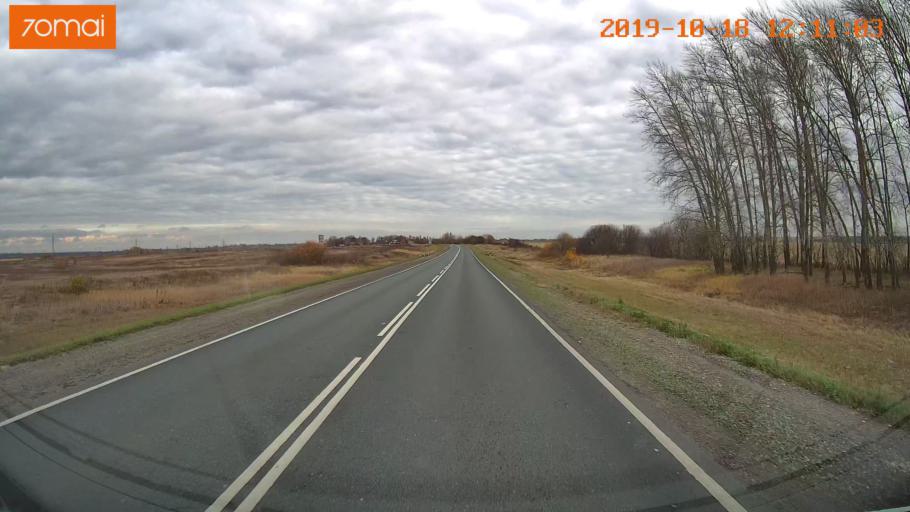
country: RU
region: Rjazan
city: Zakharovo
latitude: 54.3977
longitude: 39.3441
